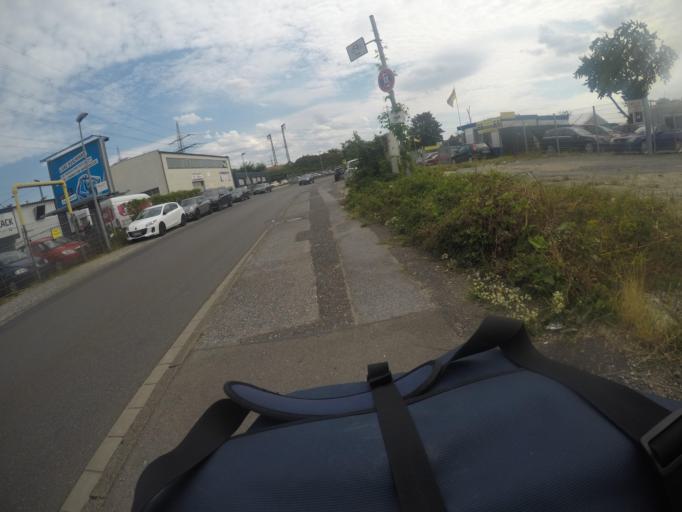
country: DE
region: North Rhine-Westphalia
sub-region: Regierungsbezirk Dusseldorf
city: Dusseldorf
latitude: 51.2204
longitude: 6.8381
